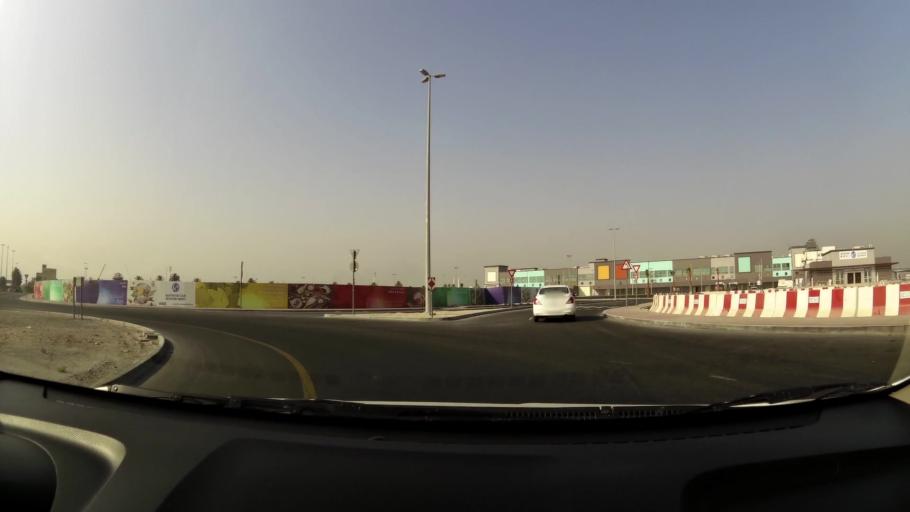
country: AE
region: Ash Shariqah
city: Sharjah
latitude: 25.2941
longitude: 55.3256
